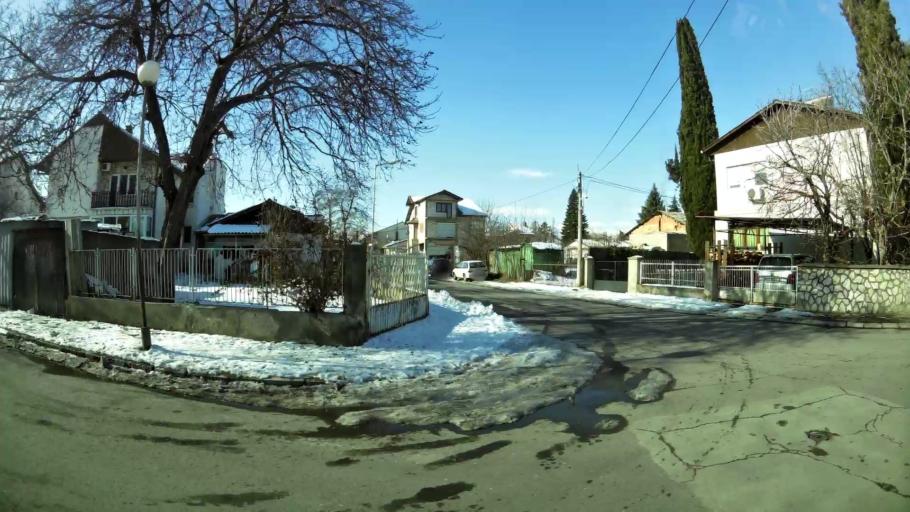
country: MK
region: Saraj
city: Saraj
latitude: 42.0050
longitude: 21.3501
